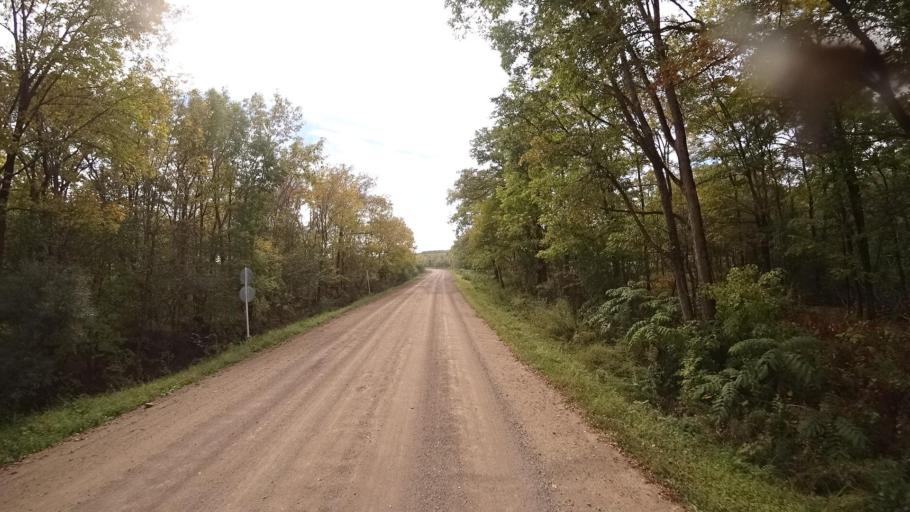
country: RU
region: Primorskiy
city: Yakovlevka
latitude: 44.5318
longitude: 133.6009
